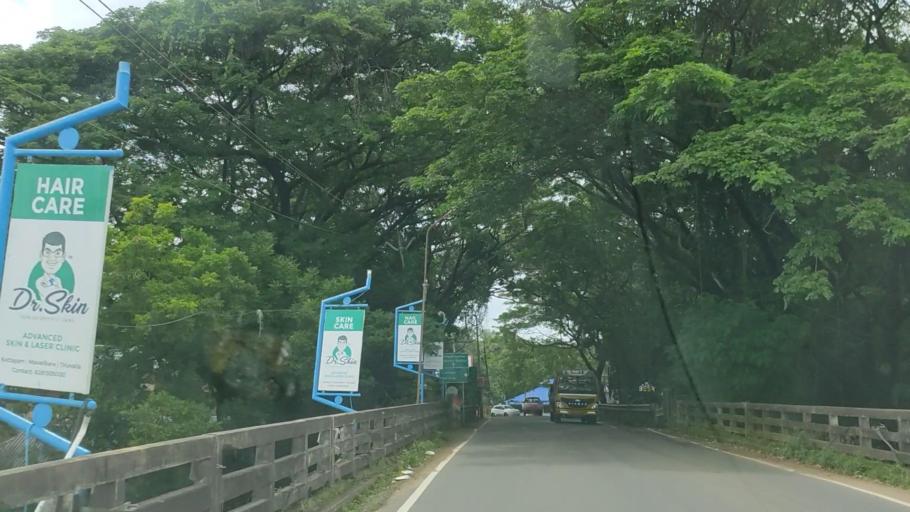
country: IN
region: Kerala
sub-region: Alappuzha
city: Shertallai
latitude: 9.6745
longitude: 76.3943
